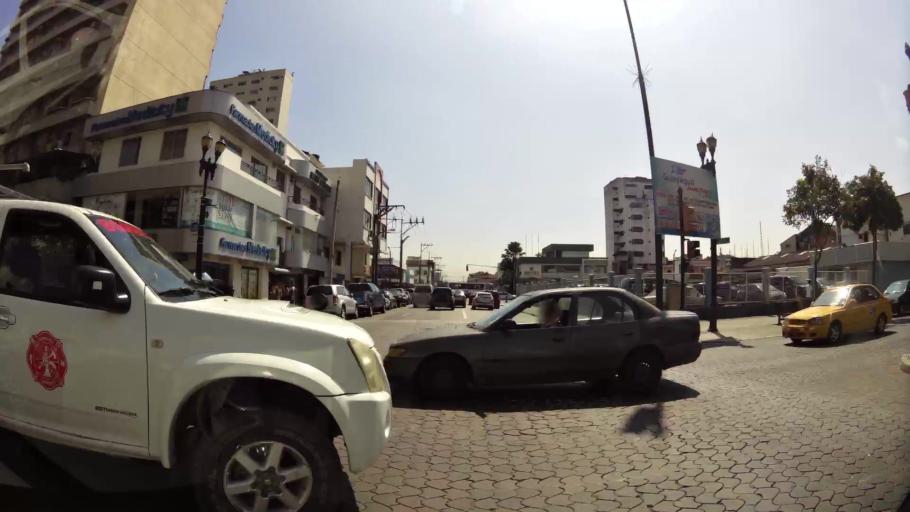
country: EC
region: Guayas
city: Guayaquil
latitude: -2.1880
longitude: -79.8933
